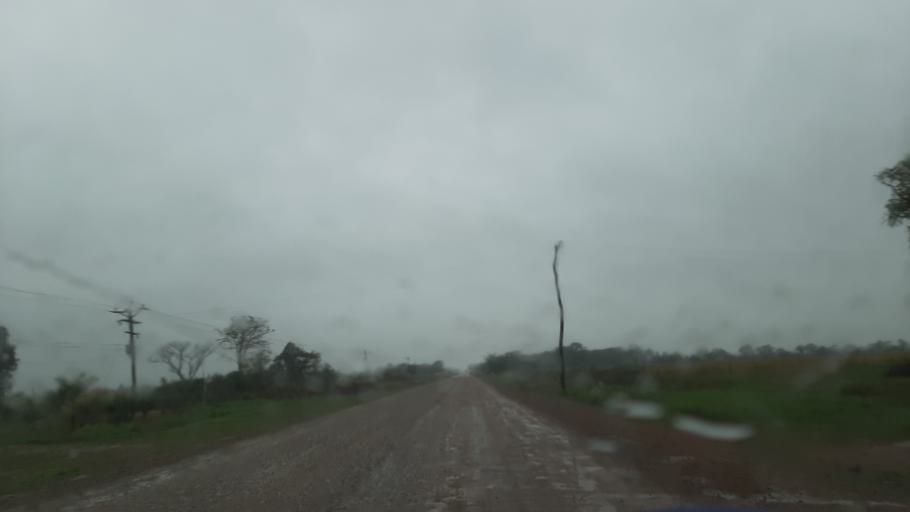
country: BO
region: Santa Cruz
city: Okinawa Numero Uno
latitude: -16.8492
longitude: -62.6090
